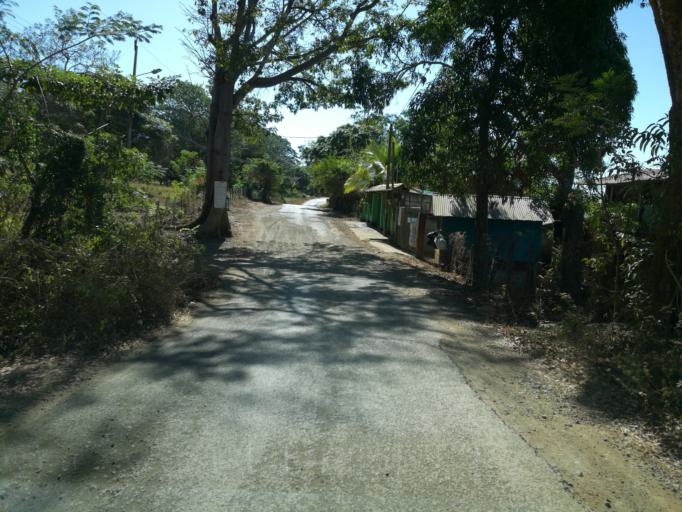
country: CR
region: Puntarenas
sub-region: Canton Central de Puntarenas
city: Puntarenas
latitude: 10.0946
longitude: -84.9784
